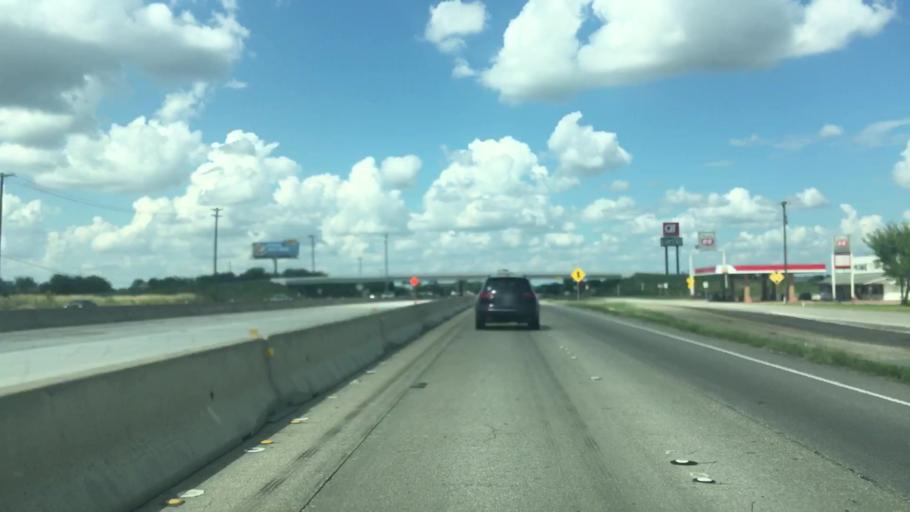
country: US
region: Texas
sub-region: Ellis County
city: Oak Leaf
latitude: 32.4572
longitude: -96.8444
